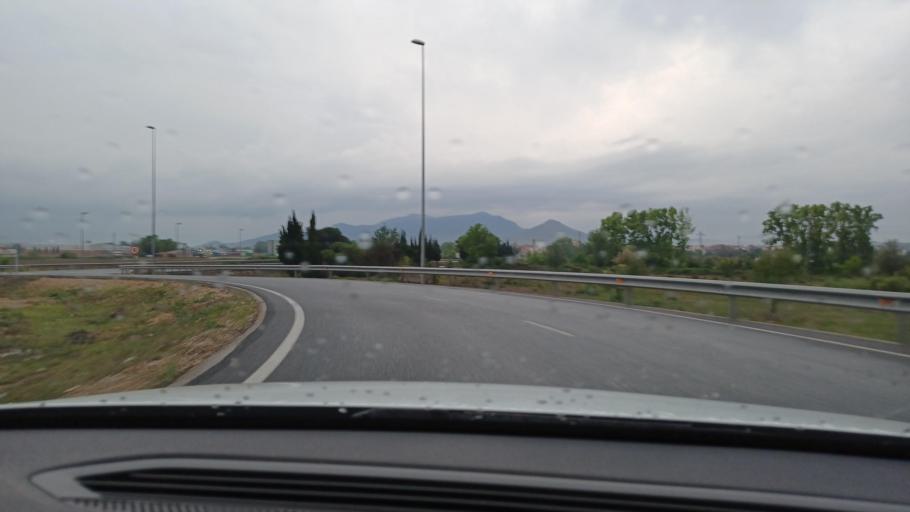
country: ES
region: Catalonia
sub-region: Provincia de Tarragona
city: Amposta
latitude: 40.7224
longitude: 0.5884
